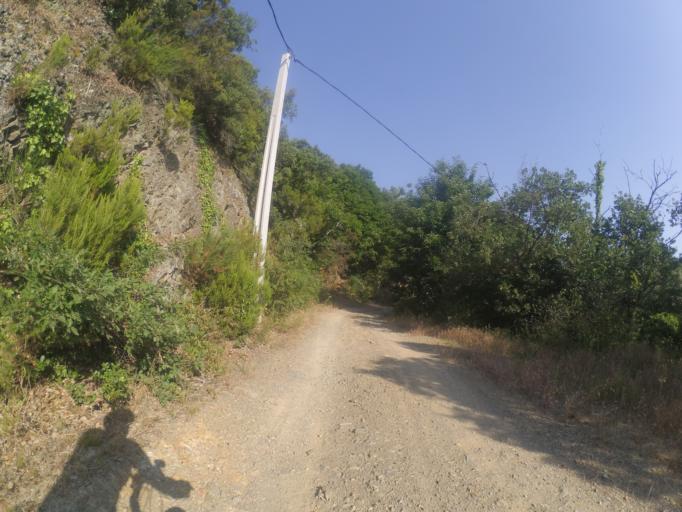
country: FR
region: Languedoc-Roussillon
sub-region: Departement des Pyrenees-Orientales
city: Ille-sur-Tet
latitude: 42.6501
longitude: 2.6487
